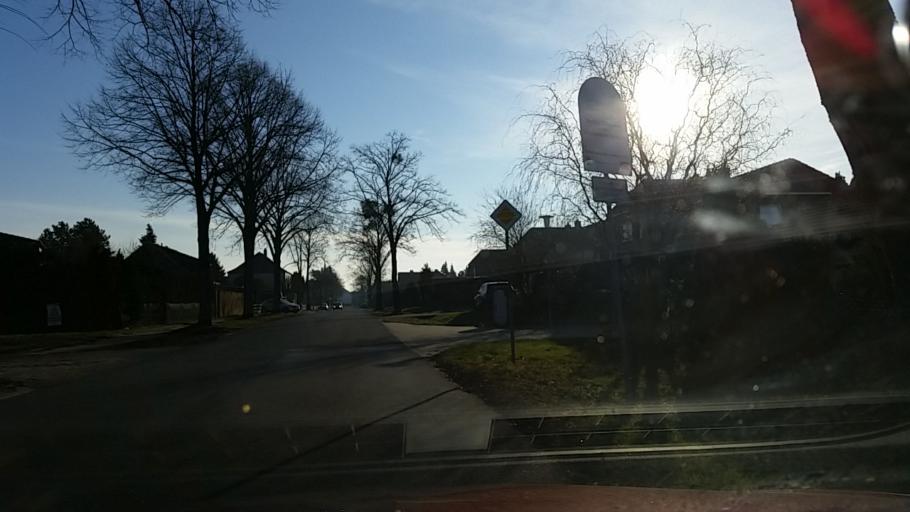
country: DE
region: Lower Saxony
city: Tiddische
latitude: 52.4865
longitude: 10.8367
